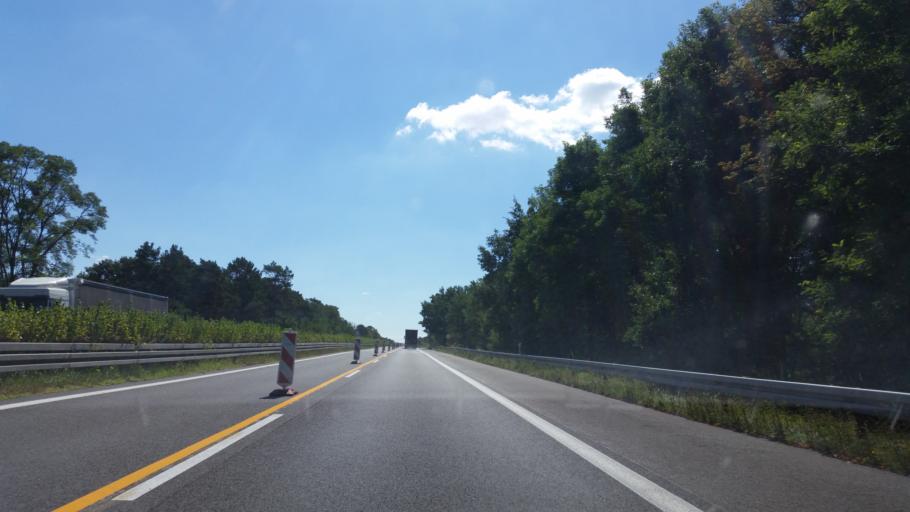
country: DE
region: Brandenburg
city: Vetschau
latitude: 51.7463
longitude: 14.1468
